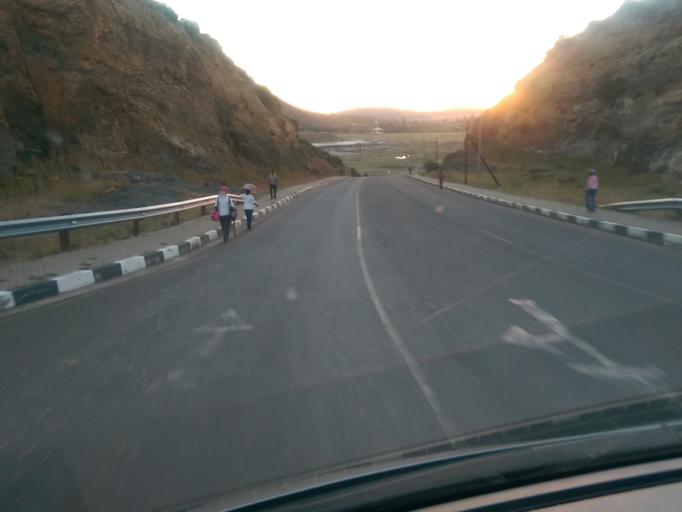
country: LS
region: Maseru
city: Maseru
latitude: -29.3291
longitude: 27.4947
